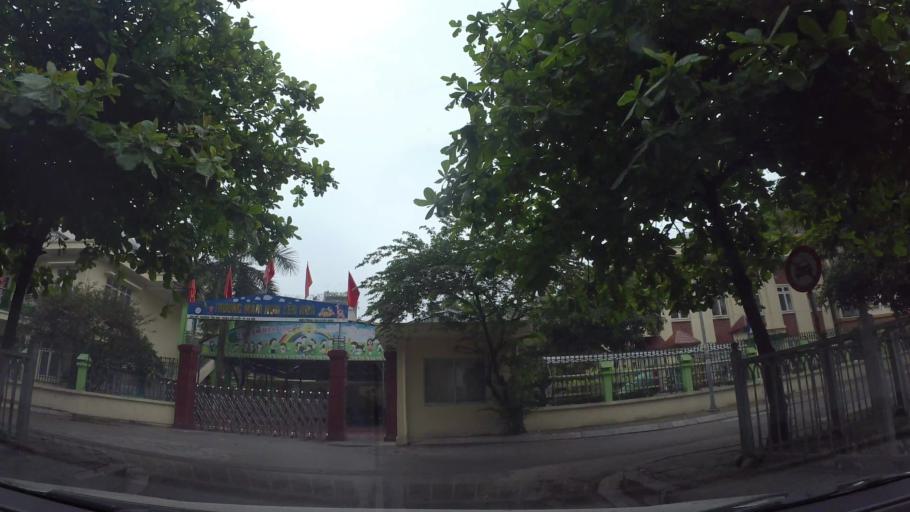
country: VN
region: Ha Noi
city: Cau Giay
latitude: 21.0204
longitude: 105.7948
